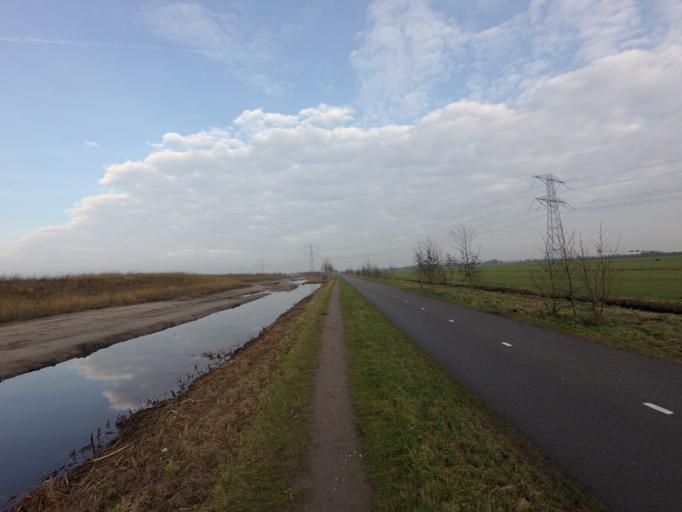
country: NL
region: Utrecht
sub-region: Gemeente Woerden
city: Woerden
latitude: 52.0797
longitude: 4.9193
